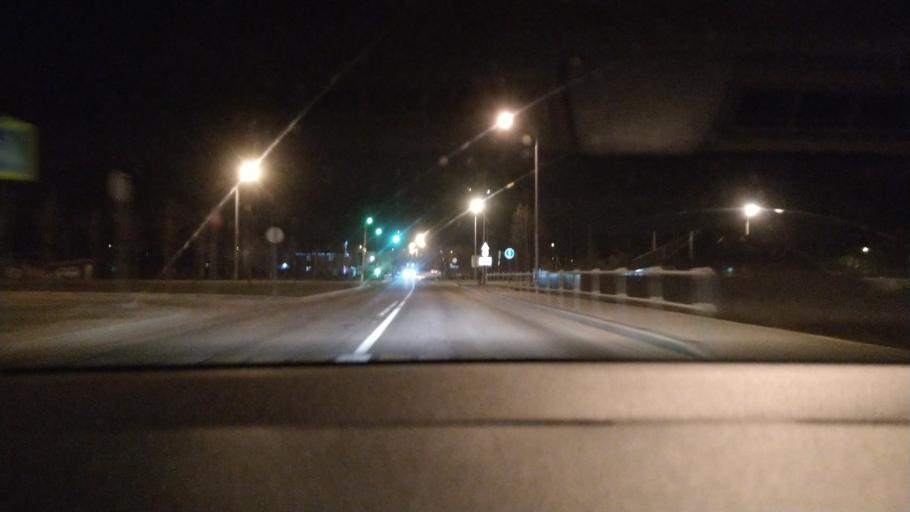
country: RU
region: Moskovskaya
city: Selyatino
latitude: 55.4823
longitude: 36.9171
